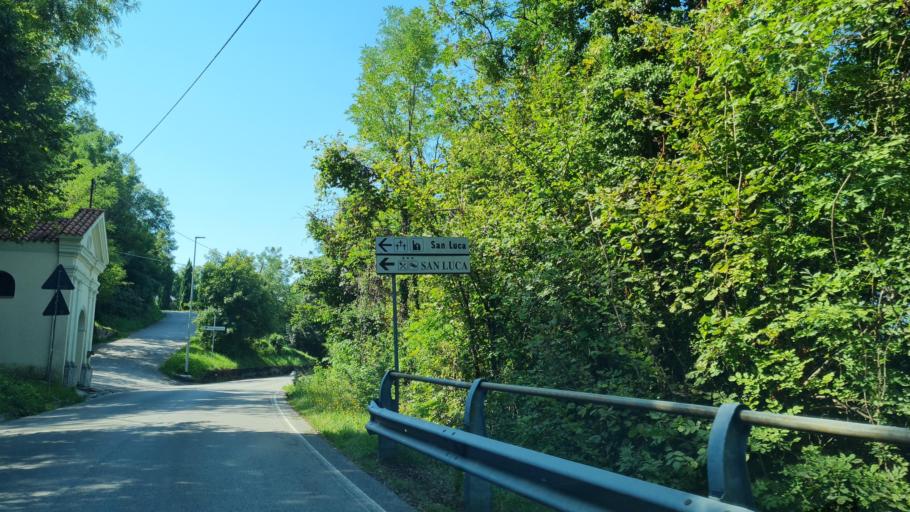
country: IT
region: Veneto
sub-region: Provincia di Vicenza
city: Conco
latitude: 45.7681
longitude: 11.6083
